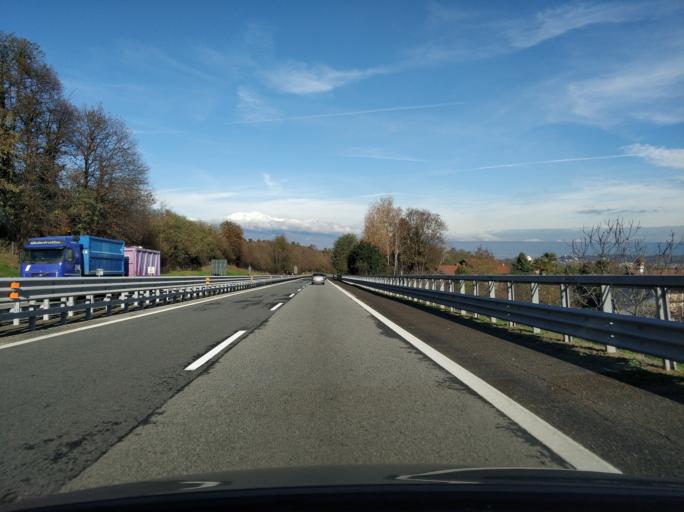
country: IT
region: Piedmont
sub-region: Provincia di Torino
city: Scarmagno
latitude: 45.3648
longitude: 7.8373
